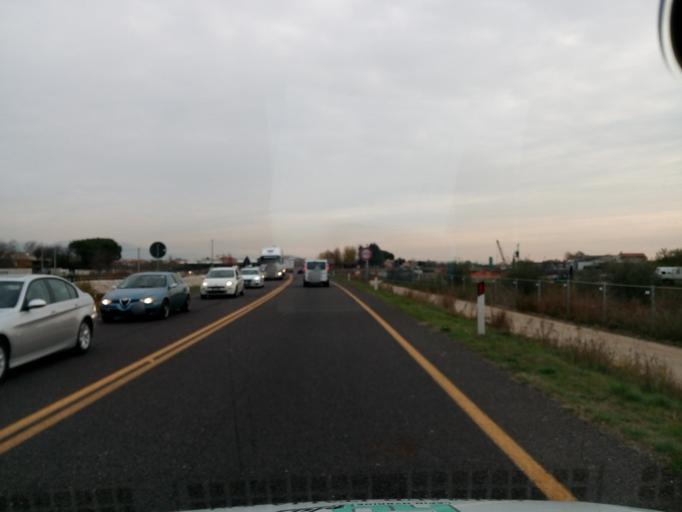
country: IT
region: Veneto
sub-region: Provincia di Vicenza
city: San Zeno-San Giuseppe
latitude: 45.7389
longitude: 11.7716
